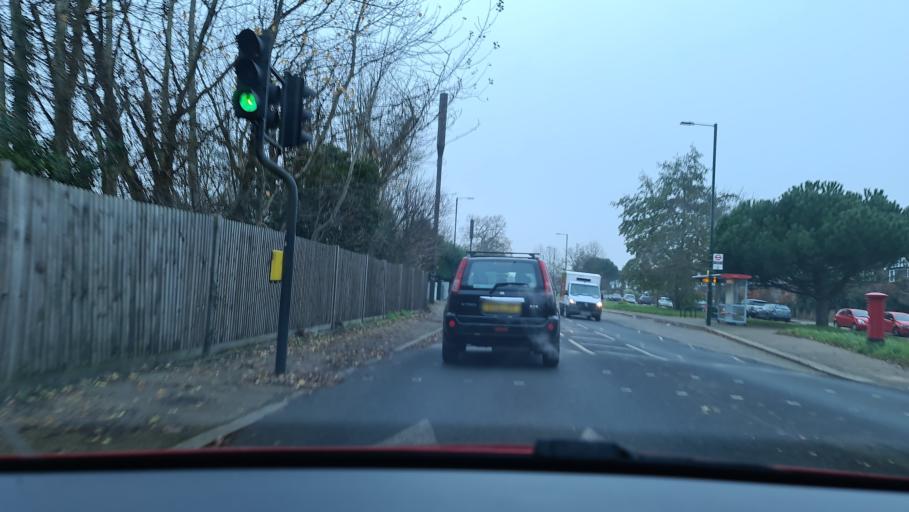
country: GB
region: England
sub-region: Greater London
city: Richmond
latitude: 51.4407
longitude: -0.3035
